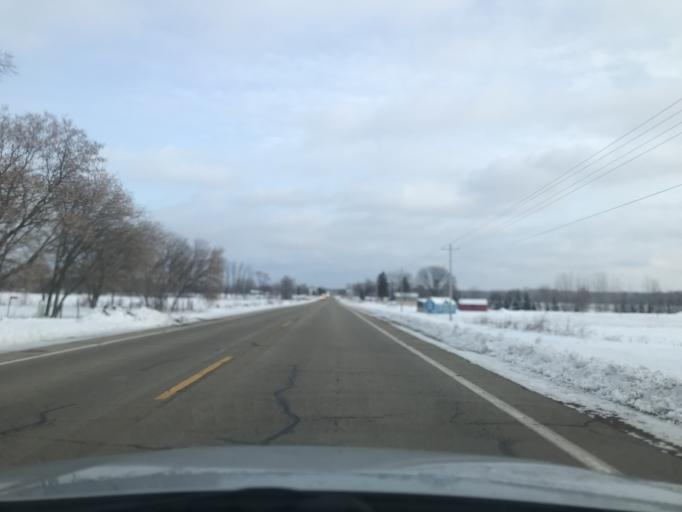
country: US
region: Wisconsin
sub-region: Oconto County
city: Oconto
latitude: 44.8925
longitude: -87.9362
